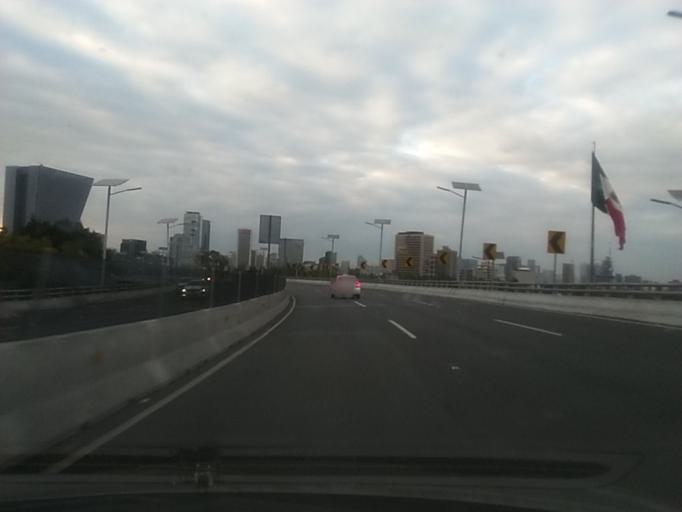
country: MX
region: Mexico City
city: Polanco
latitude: 19.4214
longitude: -99.1960
